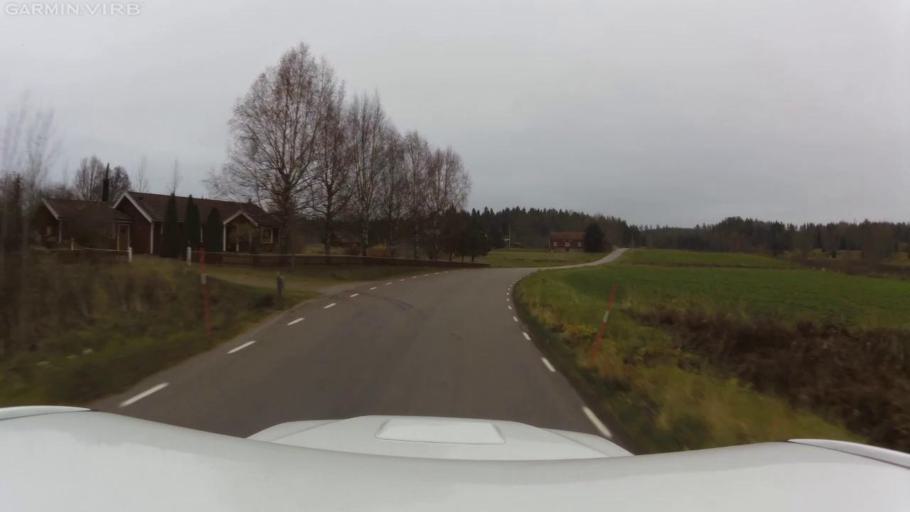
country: SE
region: OEstergoetland
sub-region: Linkopings Kommun
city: Vikingstad
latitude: 58.2198
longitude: 15.3991
